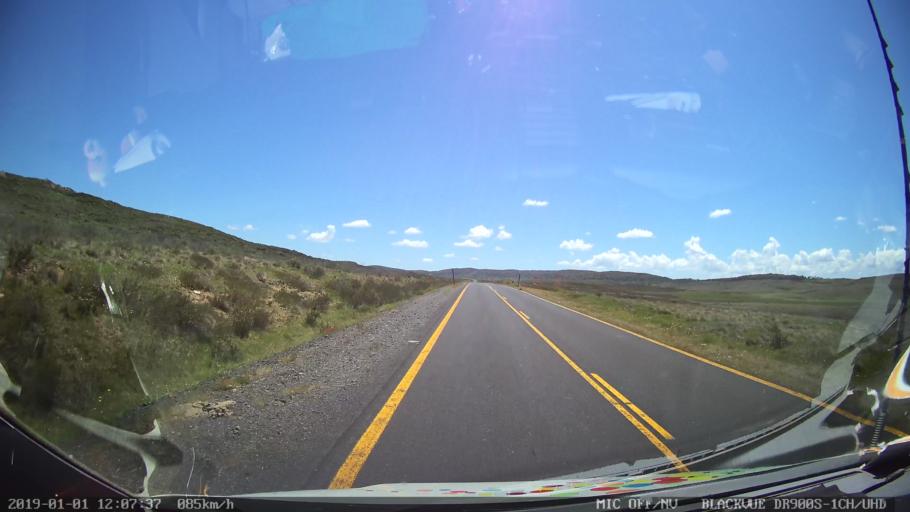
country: AU
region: New South Wales
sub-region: Tumut Shire
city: Tumut
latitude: -35.8305
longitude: 148.4906
